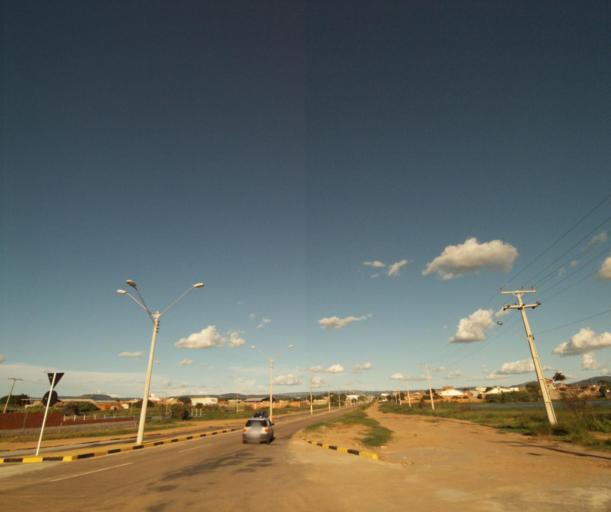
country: BR
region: Bahia
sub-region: Guanambi
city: Guanambi
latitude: -14.2101
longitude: -42.7804
